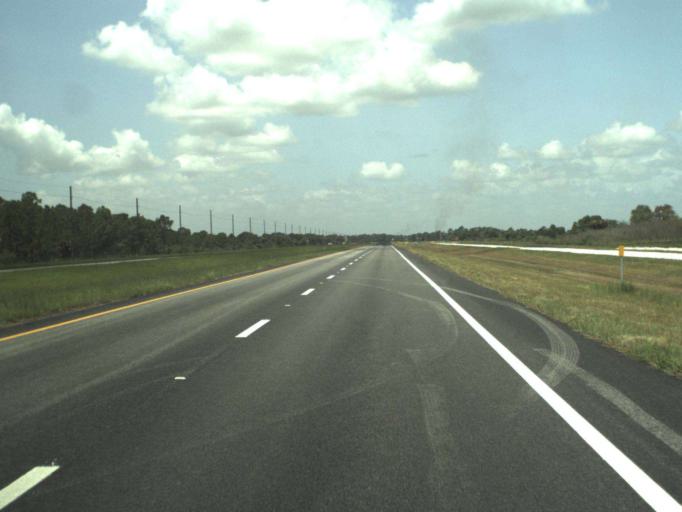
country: US
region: Florida
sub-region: Okeechobee County
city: Taylor Creek
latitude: 27.3647
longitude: -80.6120
